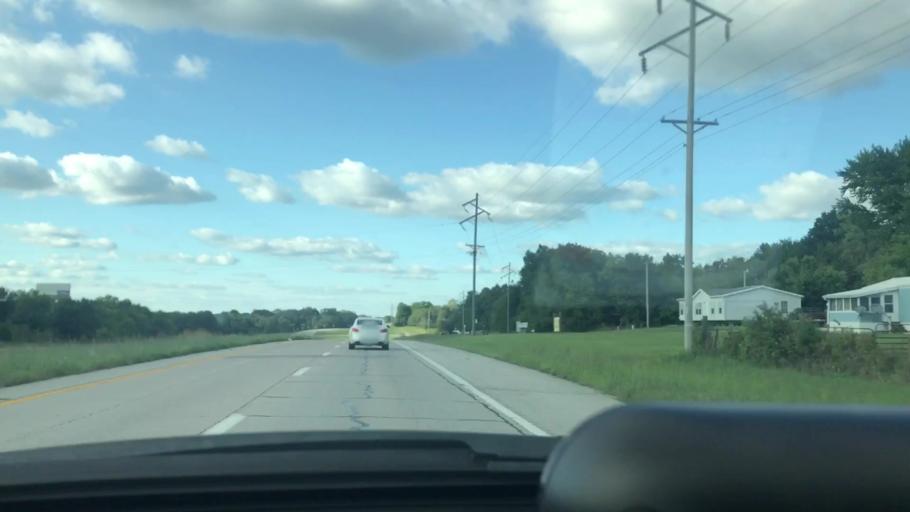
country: US
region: Missouri
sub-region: Pettis County
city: Sedalia
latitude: 38.6289
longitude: -93.2672
